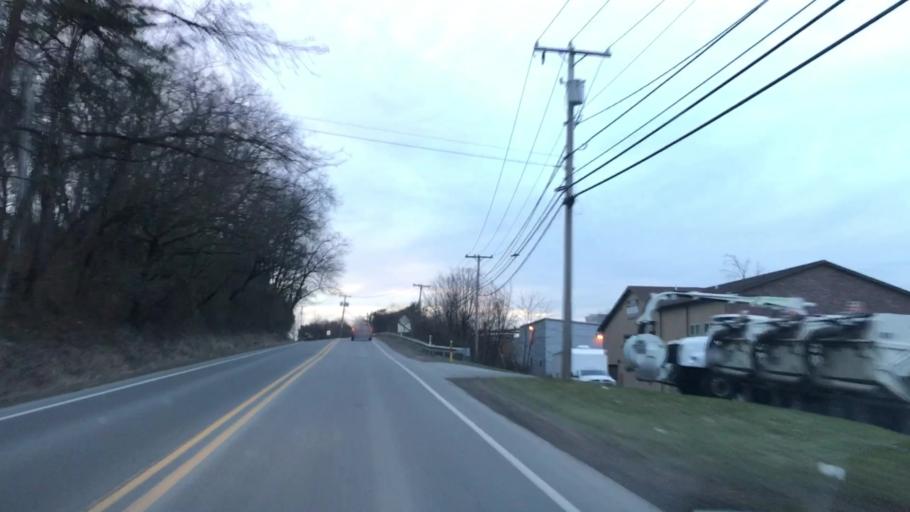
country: US
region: Pennsylvania
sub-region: Butler County
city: Mars
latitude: 40.6821
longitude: -80.0017
